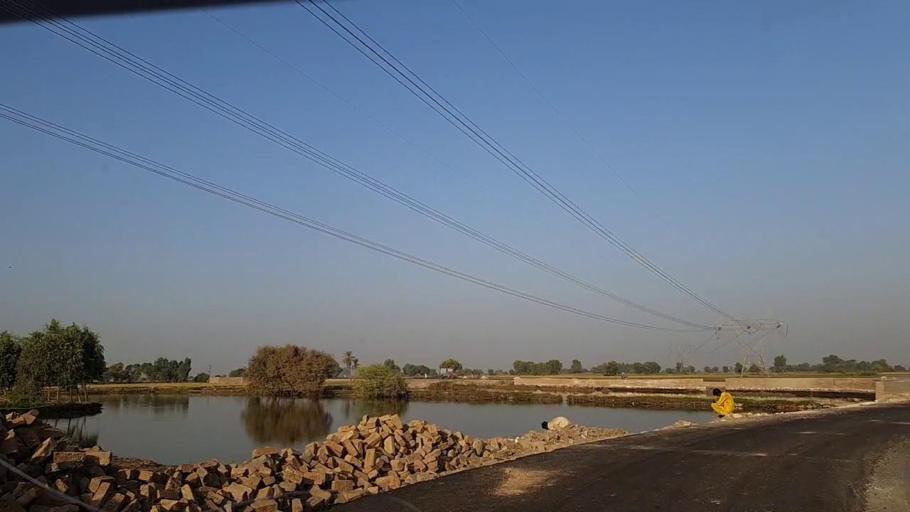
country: PK
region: Sindh
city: Rustam jo Goth
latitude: 27.9695
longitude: 68.8020
